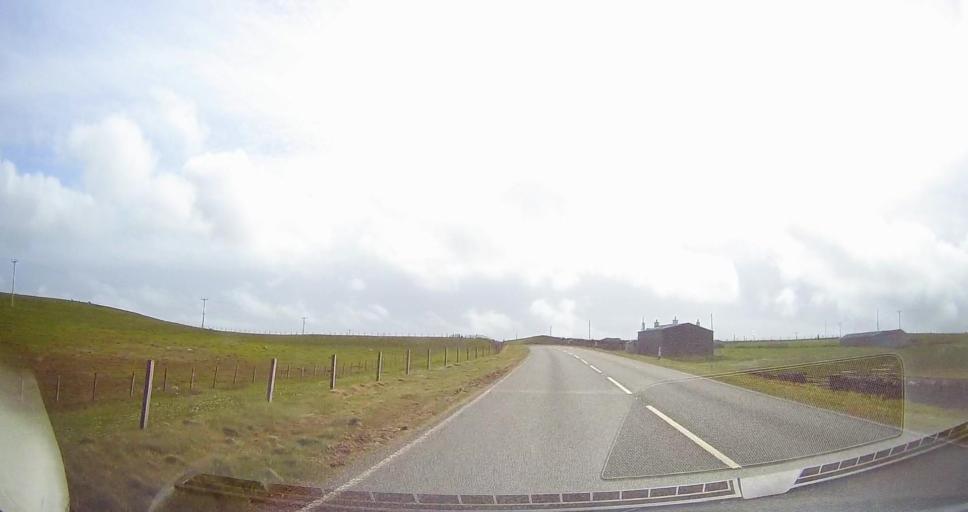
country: GB
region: Scotland
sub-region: Shetland Islands
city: Sandwick
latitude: 59.9148
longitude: -1.3013
